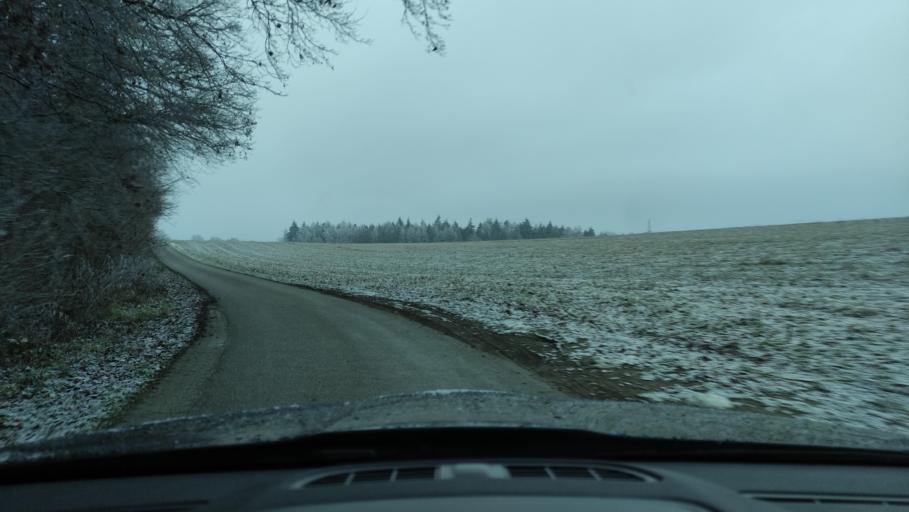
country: DE
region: Bavaria
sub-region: Swabia
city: Deisenhausen
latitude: 48.2640
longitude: 10.3400
